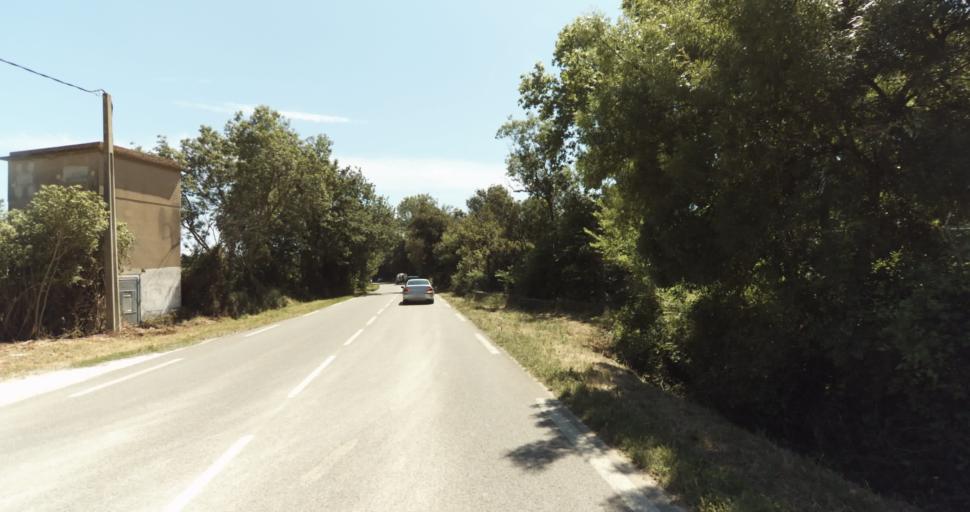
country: FR
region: Provence-Alpes-Cote d'Azur
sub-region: Departement du Var
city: Hyeres
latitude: 43.1363
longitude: 6.1573
